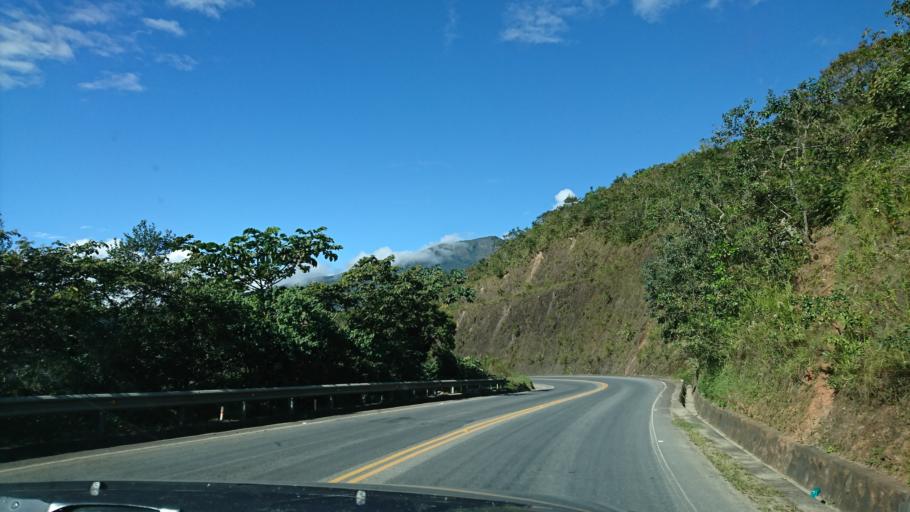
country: BO
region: La Paz
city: Coroico
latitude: -16.2050
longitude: -67.7709
